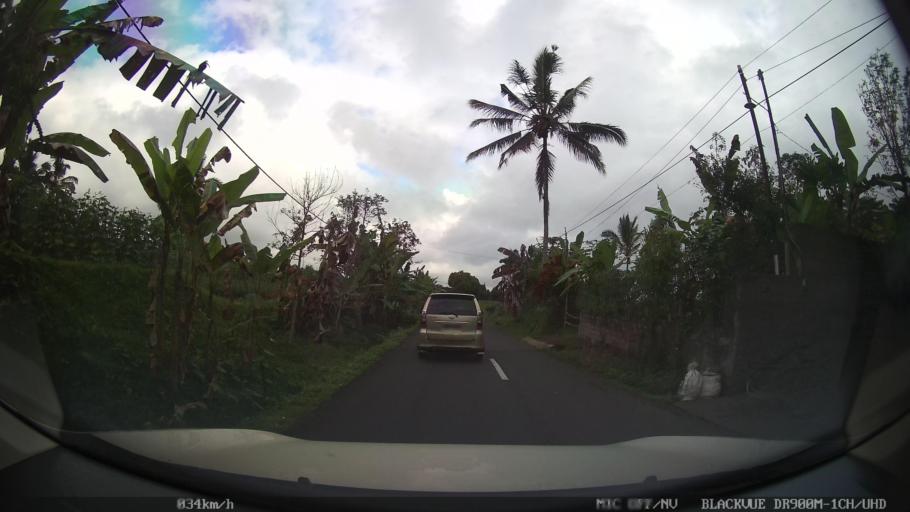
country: ID
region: Bali
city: Peneng
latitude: -8.3592
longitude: 115.1852
